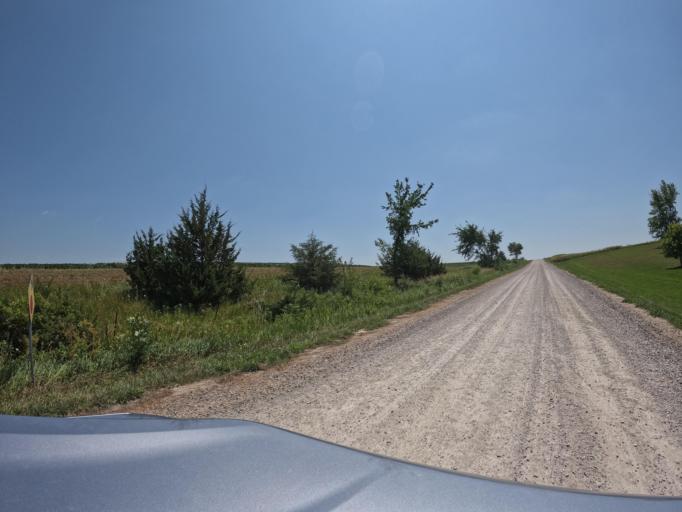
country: US
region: Iowa
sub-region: Keokuk County
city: Sigourney
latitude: 41.2748
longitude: -92.1807
